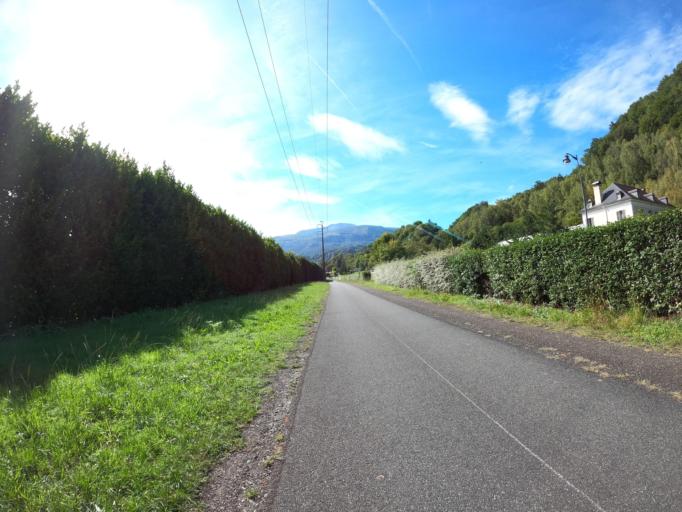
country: FR
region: Midi-Pyrenees
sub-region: Departement des Hautes-Pyrenees
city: Argeles-Gazost
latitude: 43.0160
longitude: -0.0972
